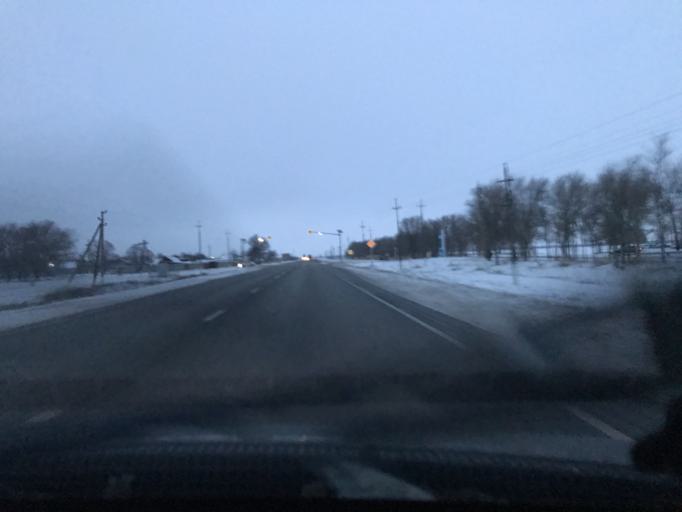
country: RU
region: Rostov
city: Letnik
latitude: 45.9058
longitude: 41.2967
